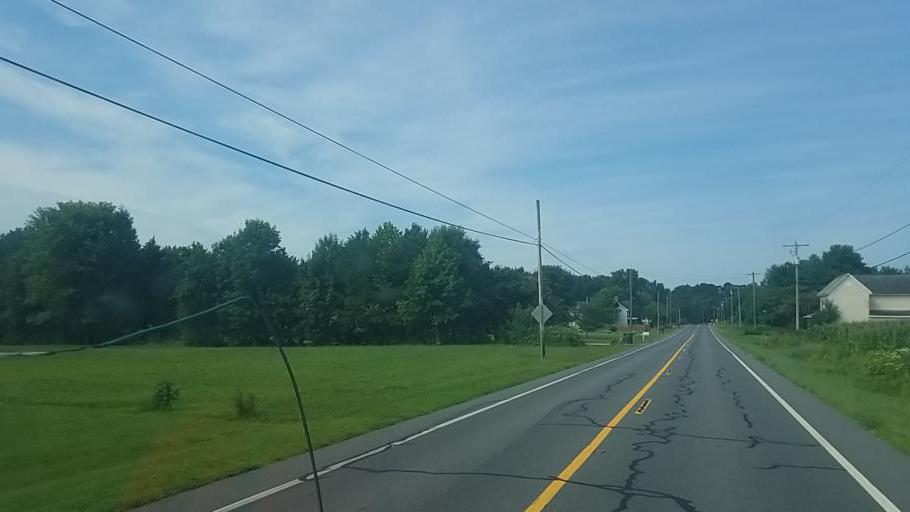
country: US
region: Delaware
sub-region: Sussex County
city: Selbyville
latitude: 38.5245
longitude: -75.2208
